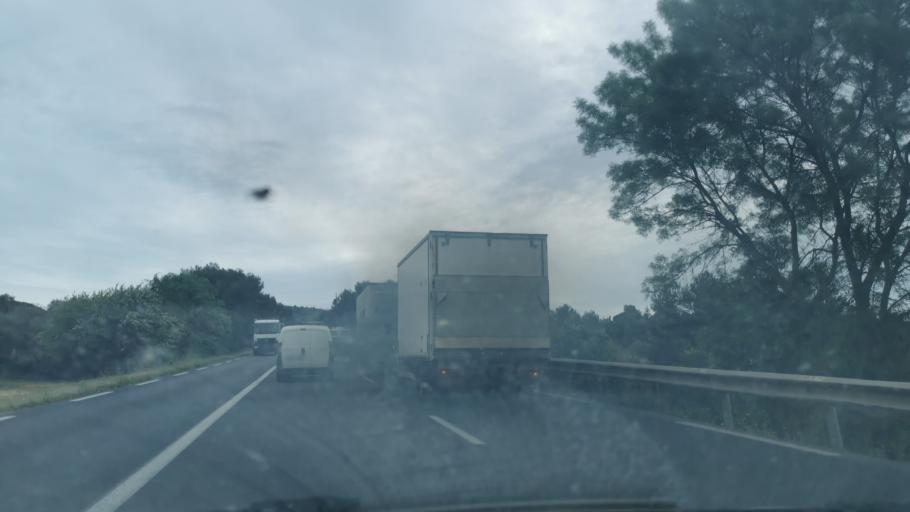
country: FR
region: Languedoc-Roussillon
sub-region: Departement de l'Herault
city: Balaruc-le-Vieux
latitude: 43.4577
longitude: 3.6988
